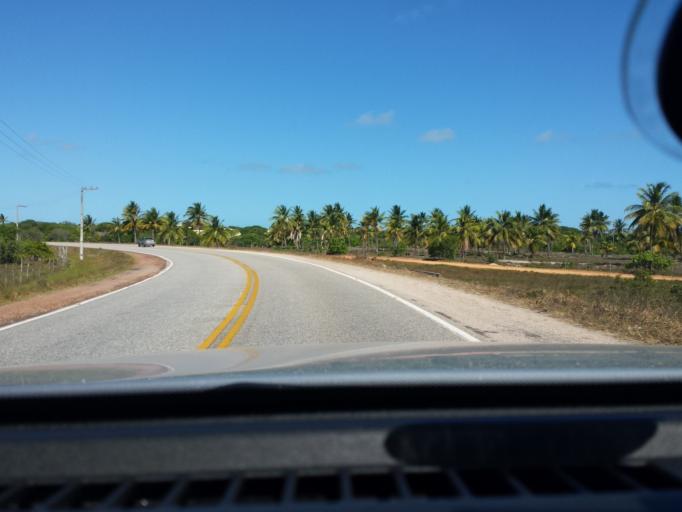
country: BR
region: Sergipe
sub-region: Estancia
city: Estancia
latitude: -11.2657
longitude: -37.2660
